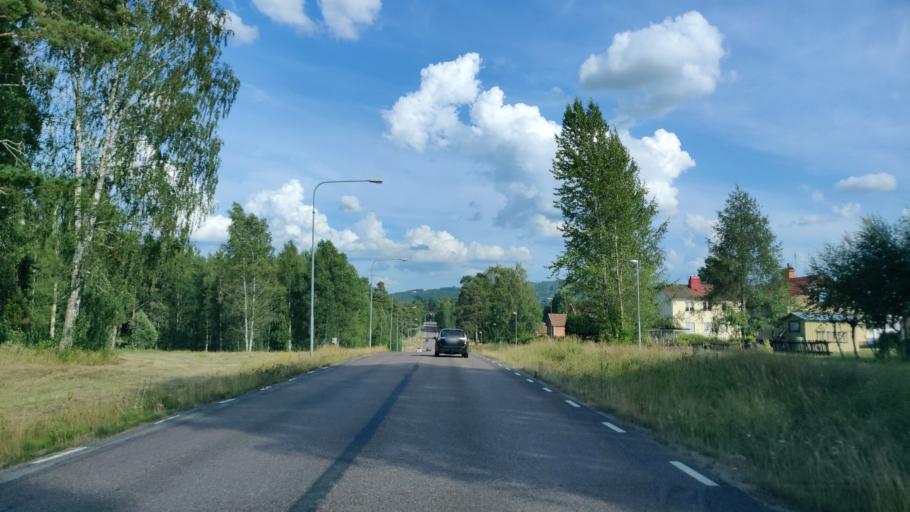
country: SE
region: Vaermland
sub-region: Hagfors Kommun
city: Hagfors
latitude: 60.0462
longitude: 13.6760
